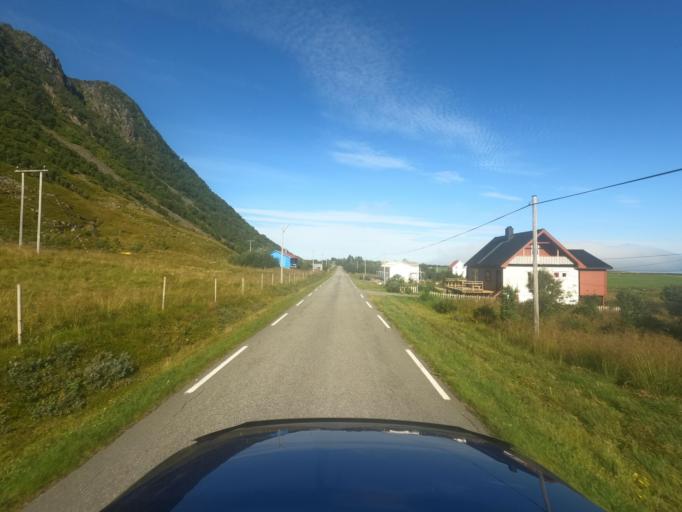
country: NO
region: Nordland
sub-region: Vestvagoy
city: Evjen
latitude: 68.3352
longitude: 13.9893
